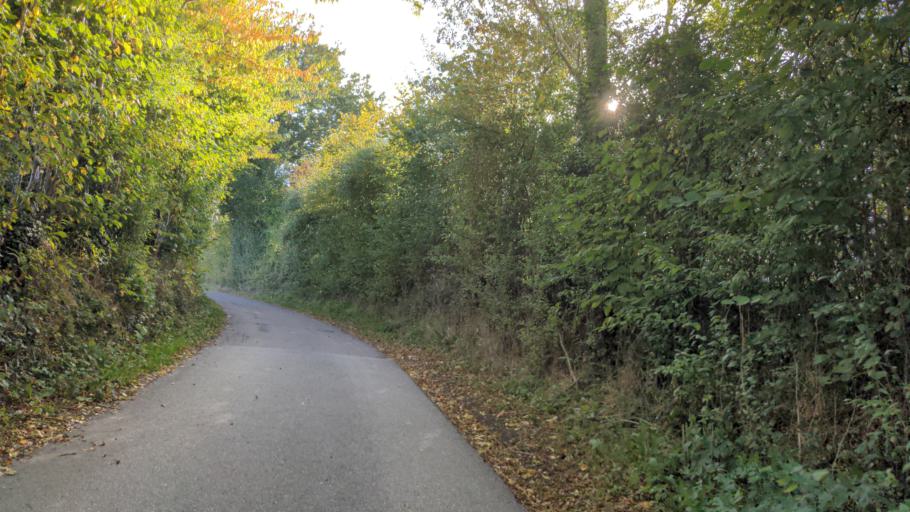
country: DE
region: Schleswig-Holstein
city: Schashagen
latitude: 54.1532
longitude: 10.9138
